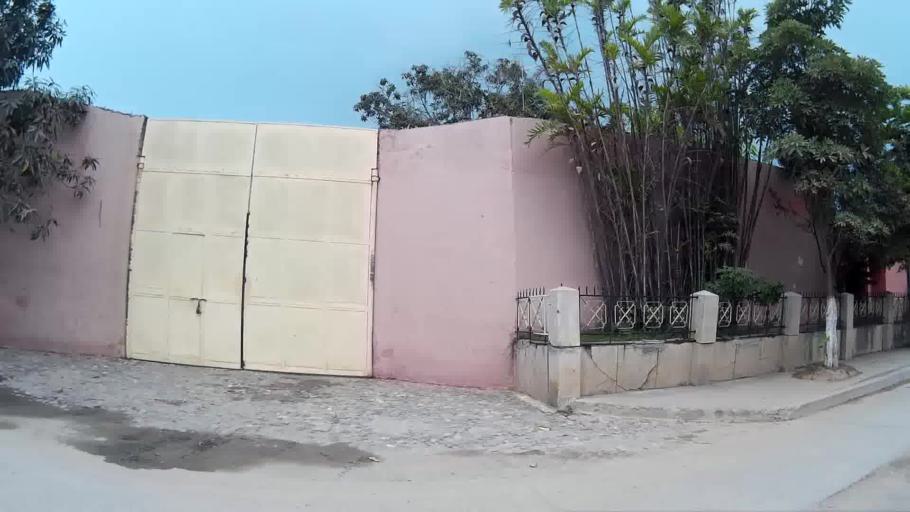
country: CO
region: Magdalena
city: Cienaga
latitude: 11.0100
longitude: -74.2448
